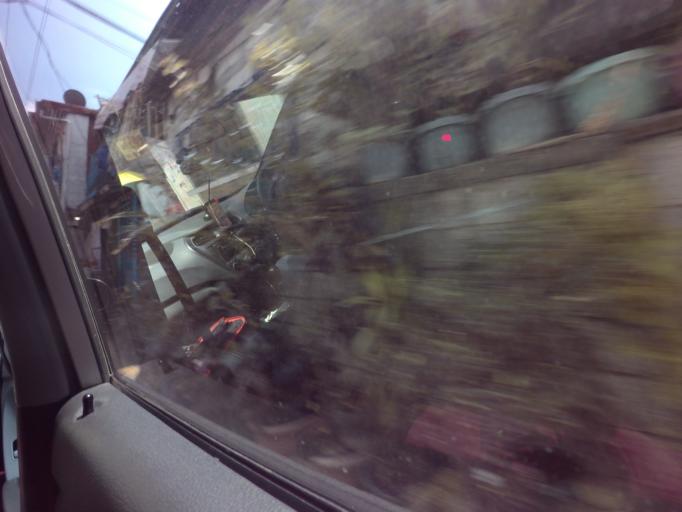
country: PH
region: Metro Manila
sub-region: San Juan
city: San Juan
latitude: 14.5929
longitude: 121.0104
